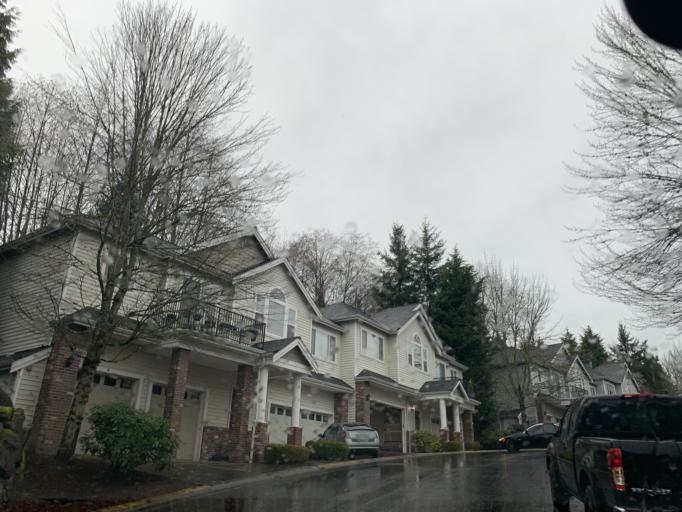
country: US
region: Washington
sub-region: King County
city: Woodinville
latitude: 47.7385
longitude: -122.1615
